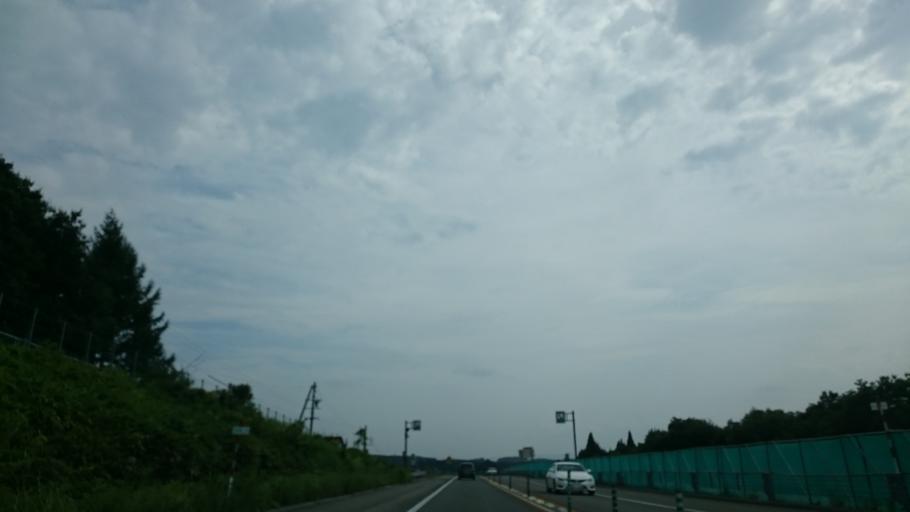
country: JP
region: Gifu
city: Gujo
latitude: 36.0062
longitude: 136.9286
